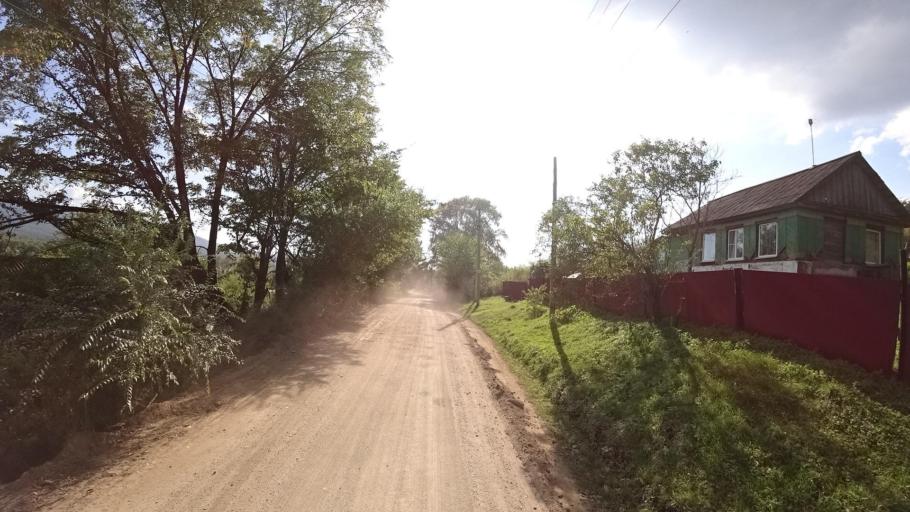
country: RU
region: Jewish Autonomous Oblast
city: Birakan
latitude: 48.9990
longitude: 131.7273
